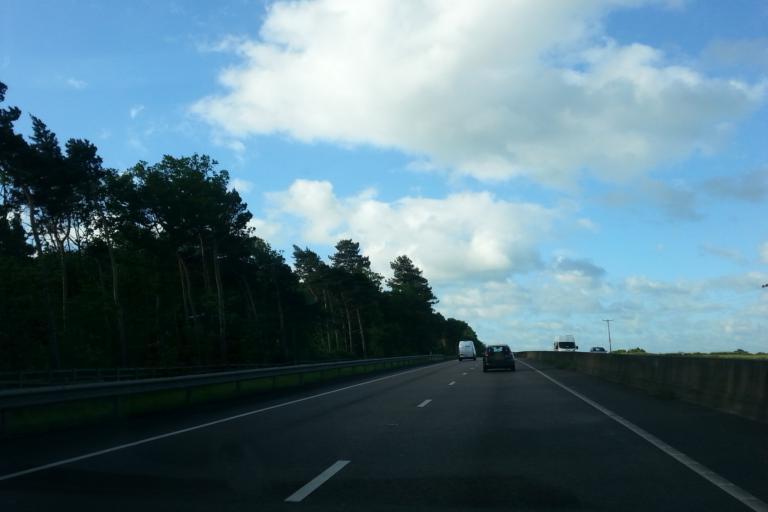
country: GB
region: England
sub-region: Nottinghamshire
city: Cotgrave
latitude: 52.8931
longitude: -1.0241
